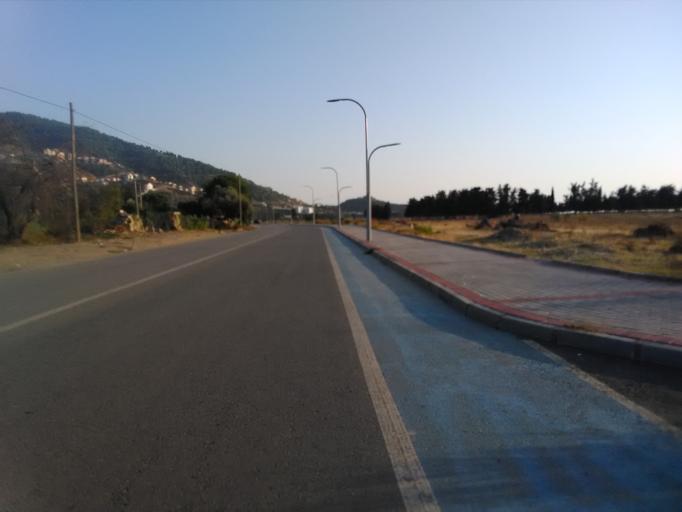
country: TR
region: Antalya
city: Gazipasa
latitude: 36.2475
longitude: 32.2948
